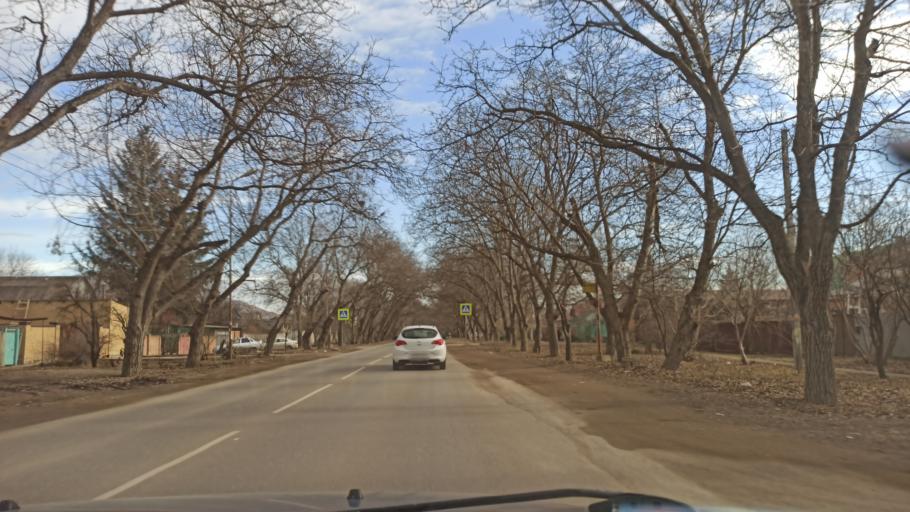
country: RU
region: Stavropol'skiy
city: Svobody
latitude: 44.0328
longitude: 43.0265
